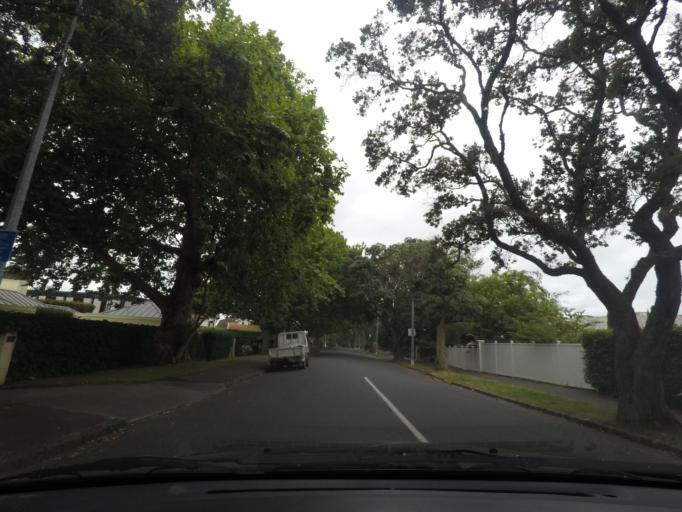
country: NZ
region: Auckland
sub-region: Auckland
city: Auckland
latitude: -36.8537
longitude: 174.7892
